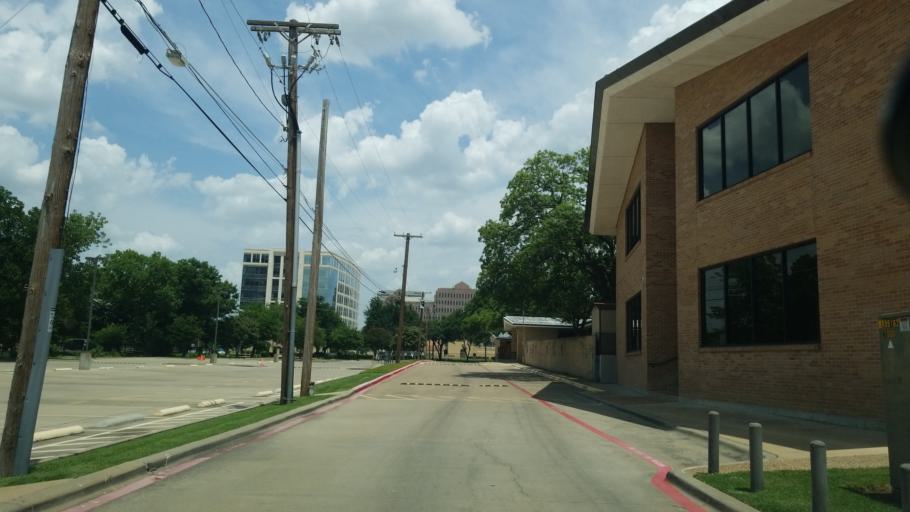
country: US
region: Texas
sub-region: Dallas County
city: University Park
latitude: 32.8609
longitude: -96.8103
